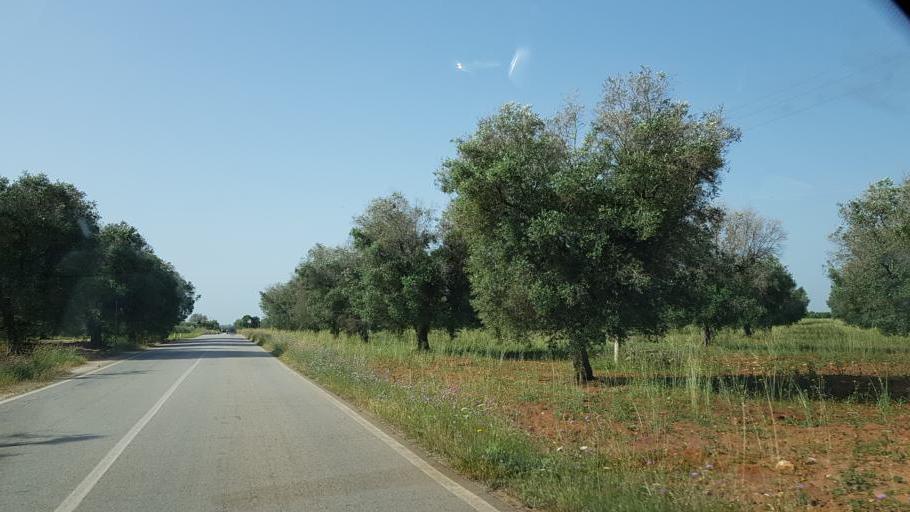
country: IT
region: Apulia
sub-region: Provincia di Brindisi
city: San Pancrazio Salentino
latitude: 40.4550
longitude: 17.8401
